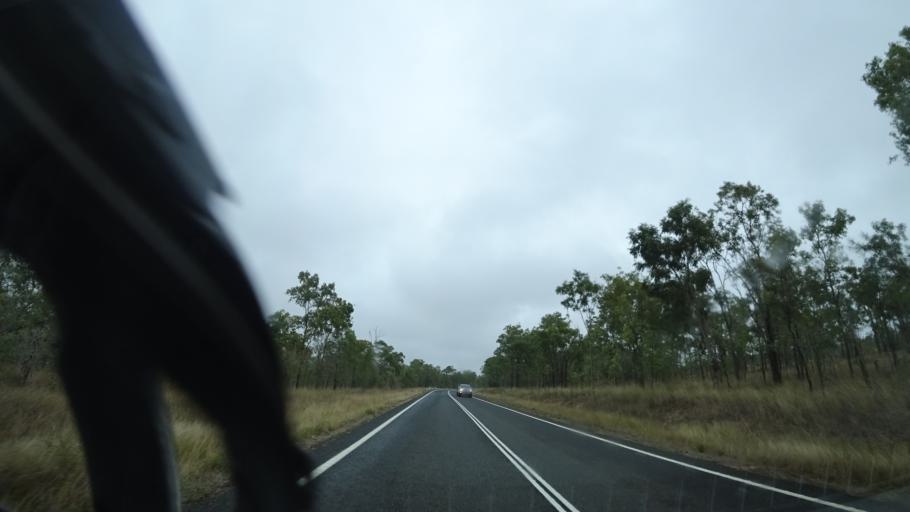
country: AU
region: Queensland
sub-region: Tablelands
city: Ravenshoe
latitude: -17.6973
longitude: 145.1822
